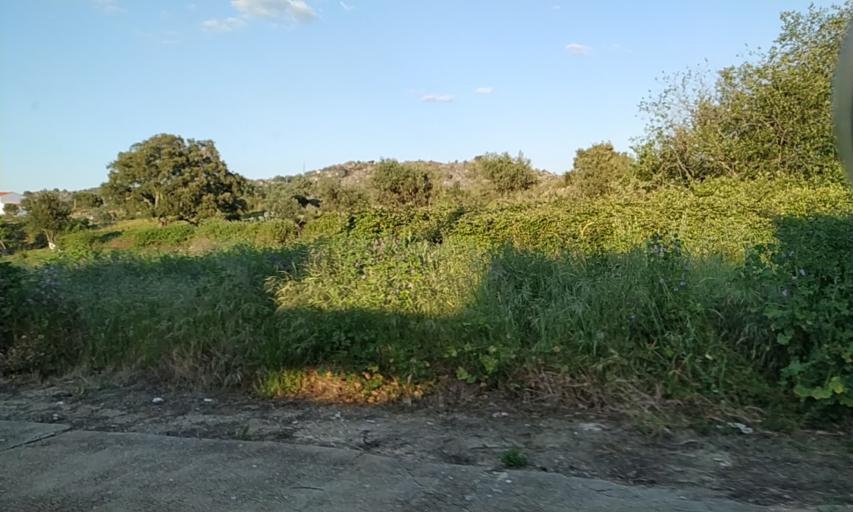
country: PT
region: Portalegre
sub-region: Portalegre
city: Sao Juliao
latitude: 39.3515
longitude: -7.2748
